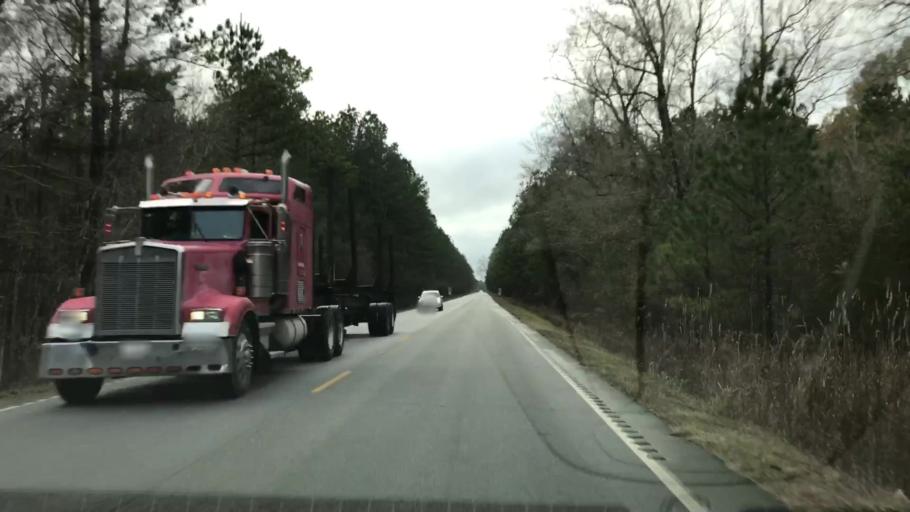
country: US
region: South Carolina
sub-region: Williamsburg County
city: Andrews
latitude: 33.2842
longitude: -79.7144
